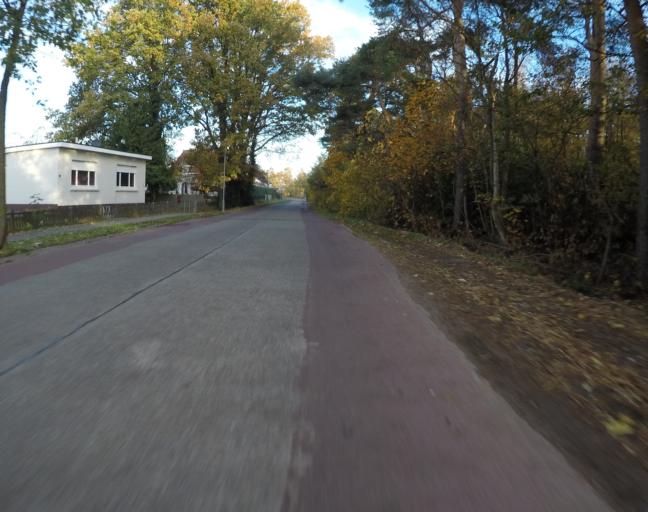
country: BE
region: Flanders
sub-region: Provincie Antwerpen
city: Herentals
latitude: 51.1650
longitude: 4.8324
